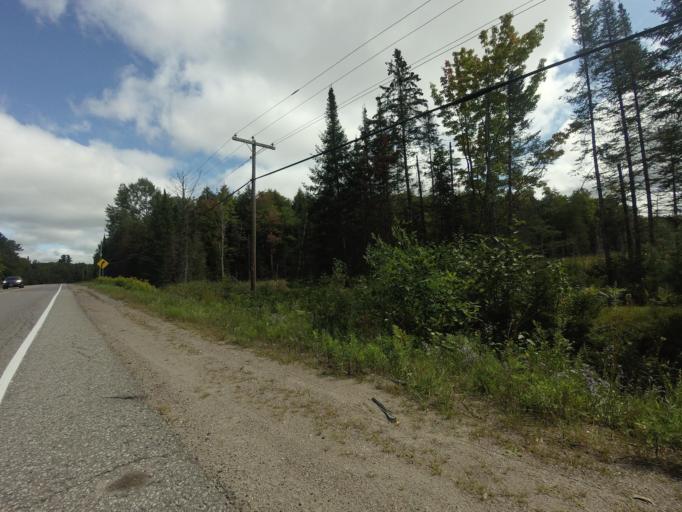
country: CA
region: Ontario
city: Omemee
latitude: 44.7960
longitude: -78.6378
